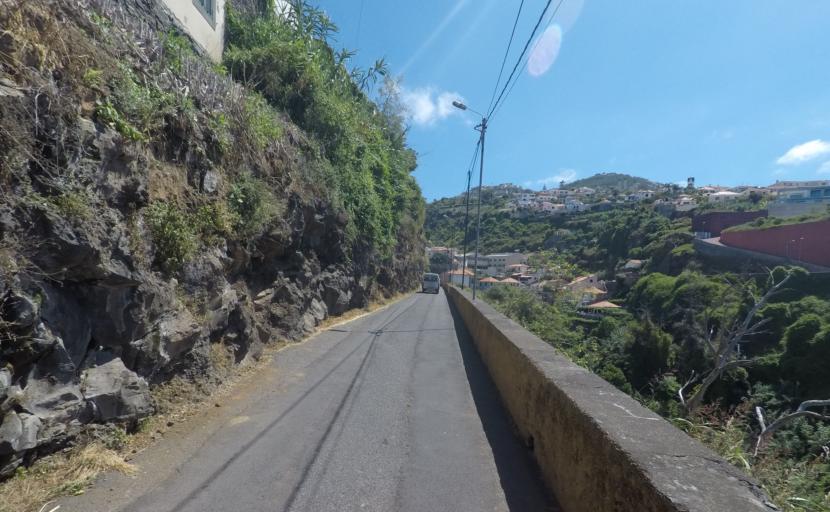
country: PT
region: Madeira
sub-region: Funchal
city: Funchal
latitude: 32.6486
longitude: -16.8877
